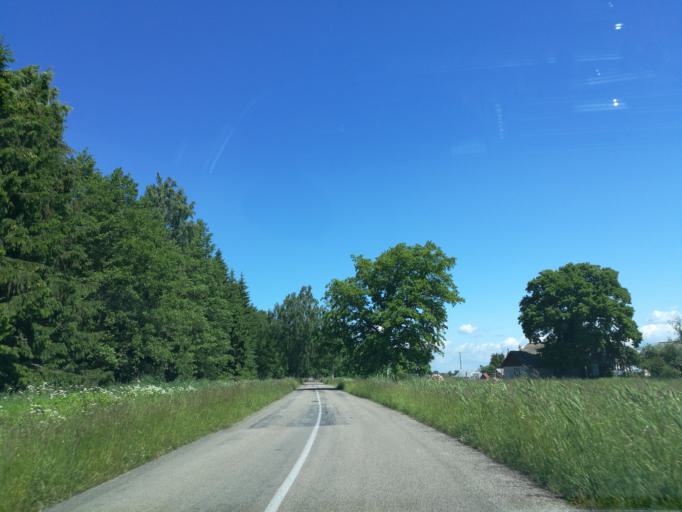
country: LT
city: Rusne
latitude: 55.3862
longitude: 21.2413
